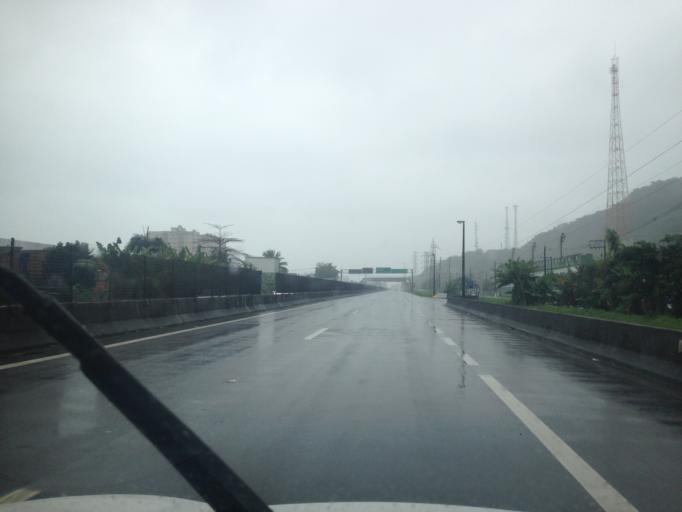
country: BR
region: Sao Paulo
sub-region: Mongagua
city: Mongagua
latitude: -24.0949
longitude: -46.6258
